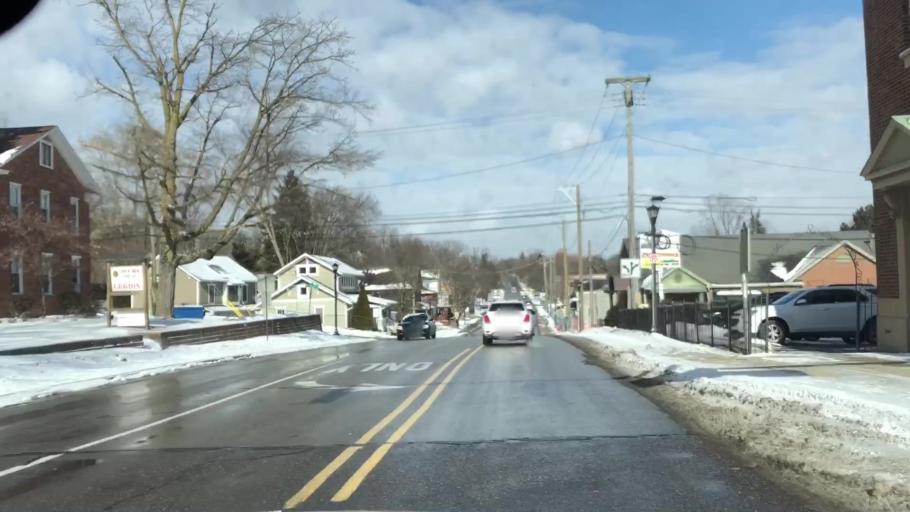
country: US
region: Michigan
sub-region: Wayne County
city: Northville
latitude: 42.4323
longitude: -83.4832
